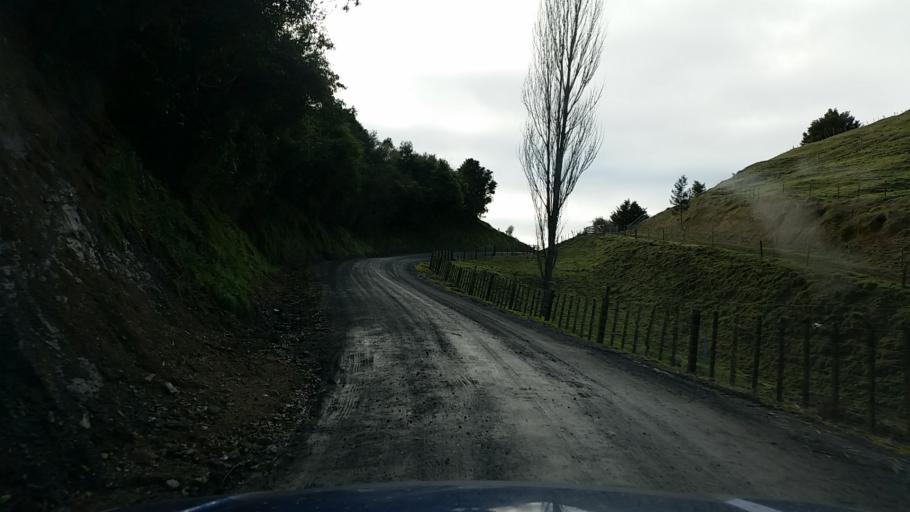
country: NZ
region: Taranaki
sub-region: New Plymouth District
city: Waitara
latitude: -39.0730
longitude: 174.7977
